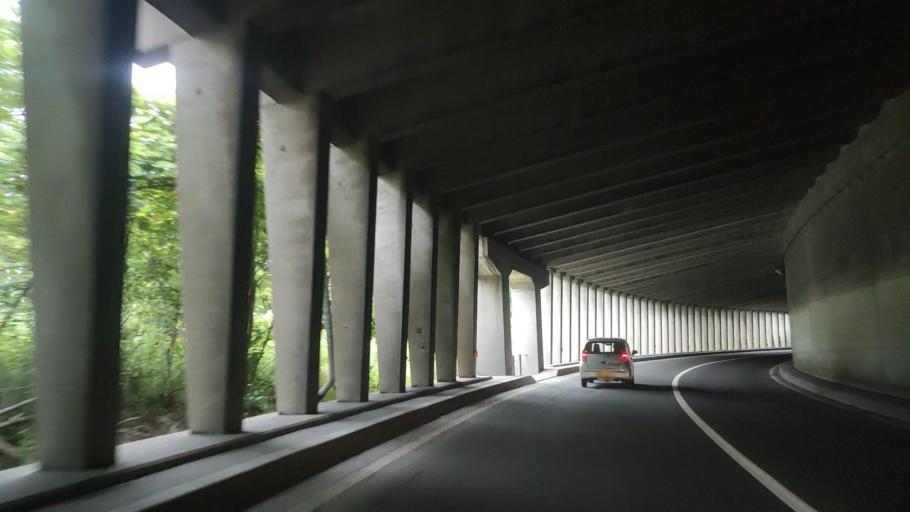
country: JP
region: Hokkaido
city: Date
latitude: 42.5649
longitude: 140.7368
